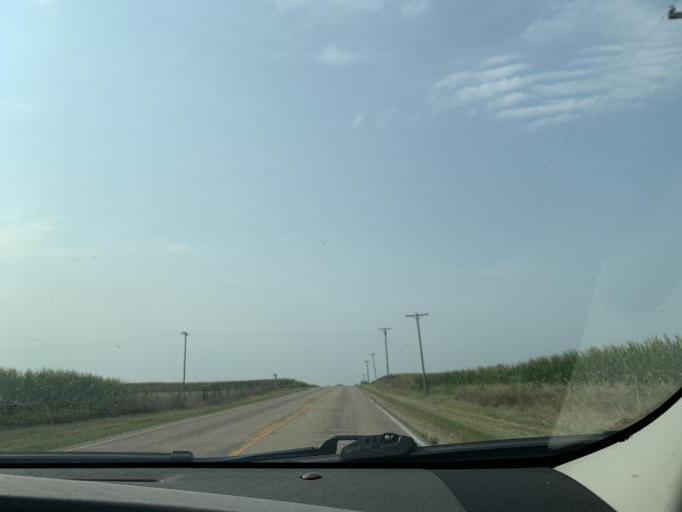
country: US
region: Illinois
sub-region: Whiteside County
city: Morrison
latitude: 41.8707
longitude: -89.9203
